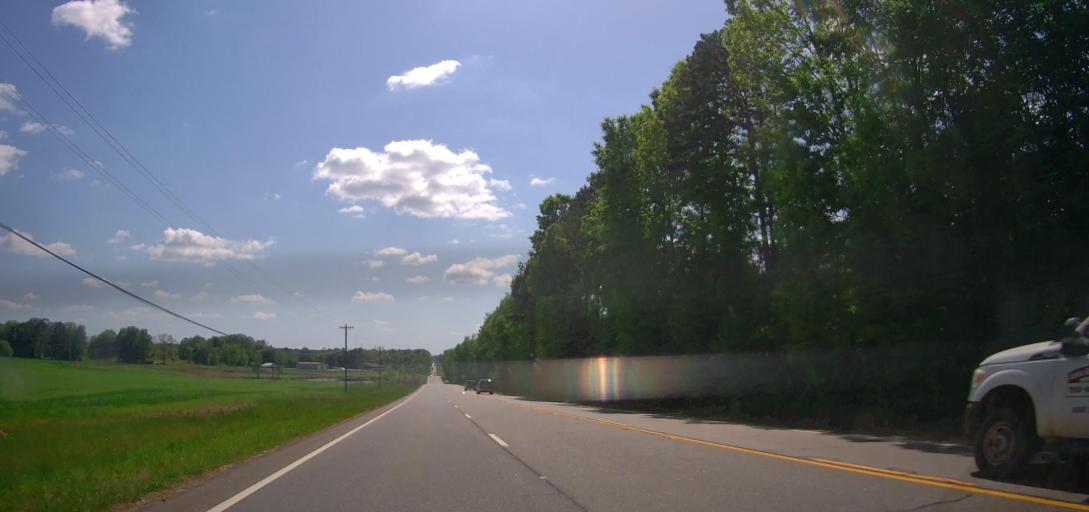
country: US
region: Georgia
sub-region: Putnam County
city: Jefferson
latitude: 33.3814
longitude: -83.3166
